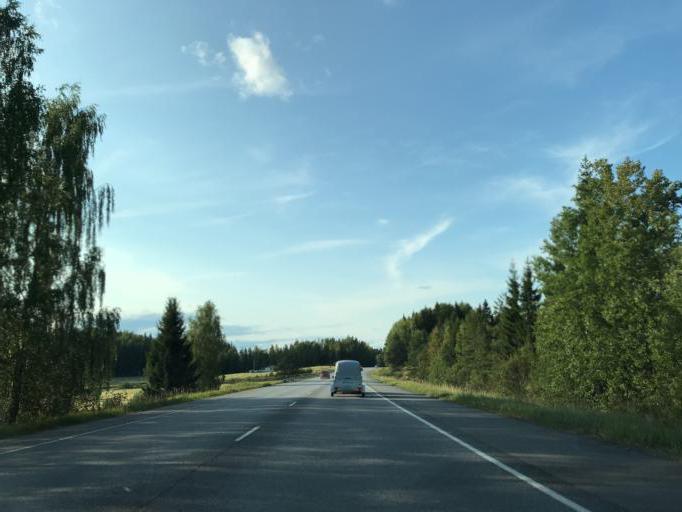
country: FI
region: Uusimaa
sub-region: Helsinki
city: Vihti
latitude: 60.3640
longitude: 24.3205
